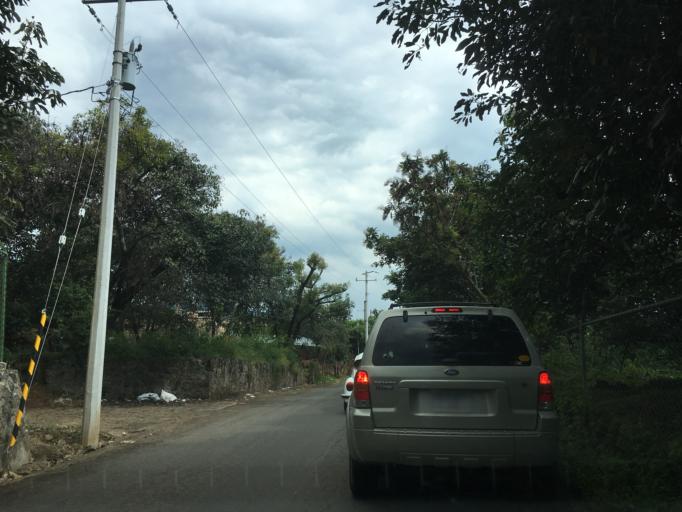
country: MX
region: Michoacan
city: Tingambato
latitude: 19.5007
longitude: -101.8584
